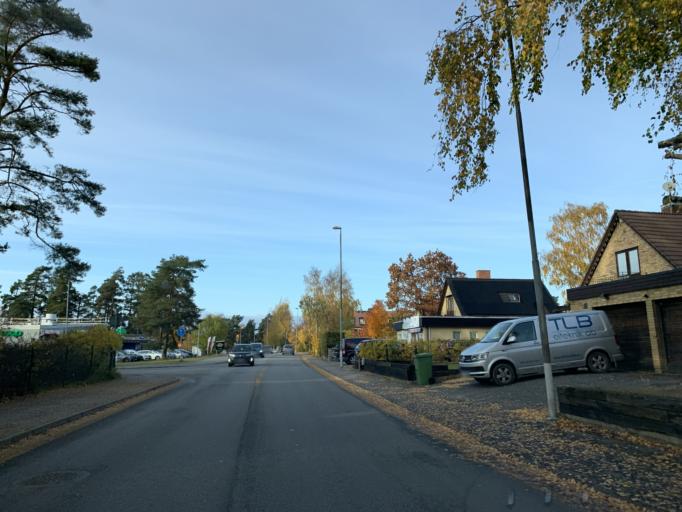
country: SE
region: Stockholm
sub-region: Haninge Kommun
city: Haninge
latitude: 59.1792
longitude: 18.1816
